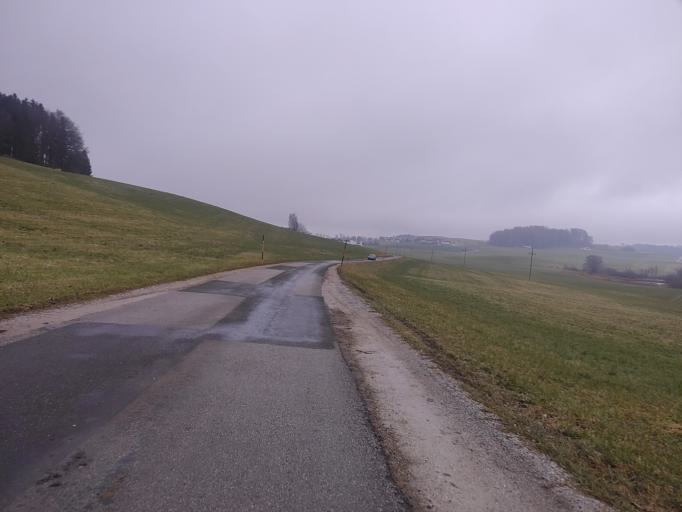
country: AT
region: Salzburg
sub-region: Politischer Bezirk Salzburg-Umgebung
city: Mattsee
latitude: 47.9635
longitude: 13.1208
